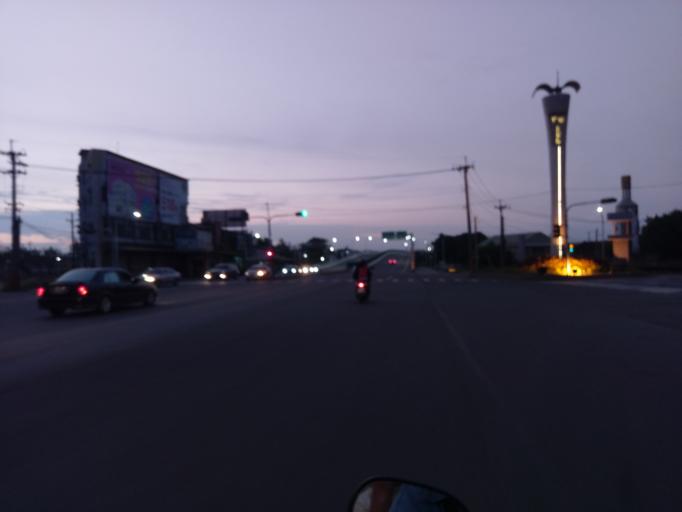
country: TW
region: Taiwan
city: Xinying
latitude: 23.1954
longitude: 120.3218
